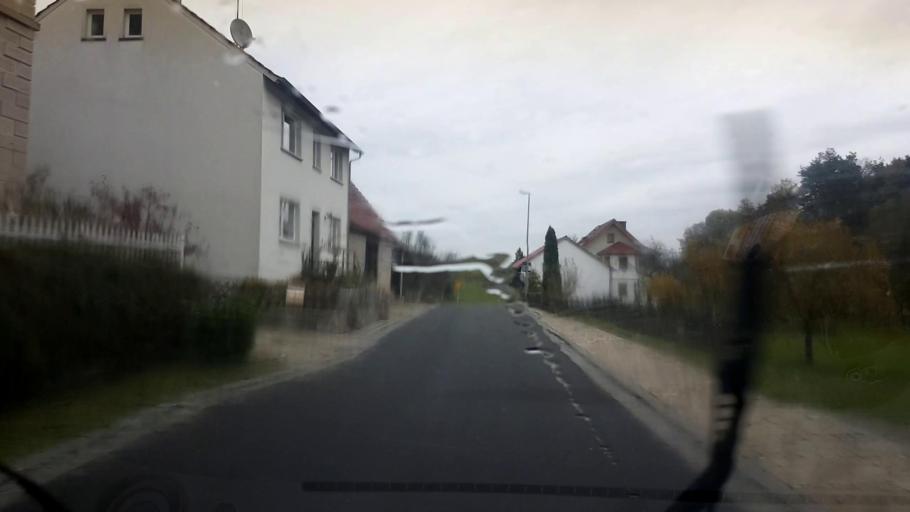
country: DE
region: Bavaria
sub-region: Upper Franconia
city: Burgwindheim
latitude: 49.8735
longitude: 10.5697
